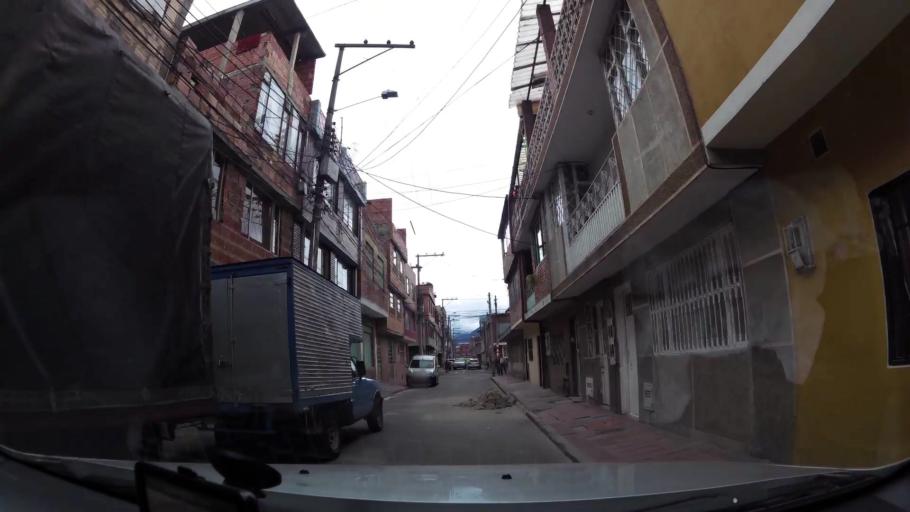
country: CO
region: Bogota D.C.
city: Bogota
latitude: 4.6038
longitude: -74.1372
